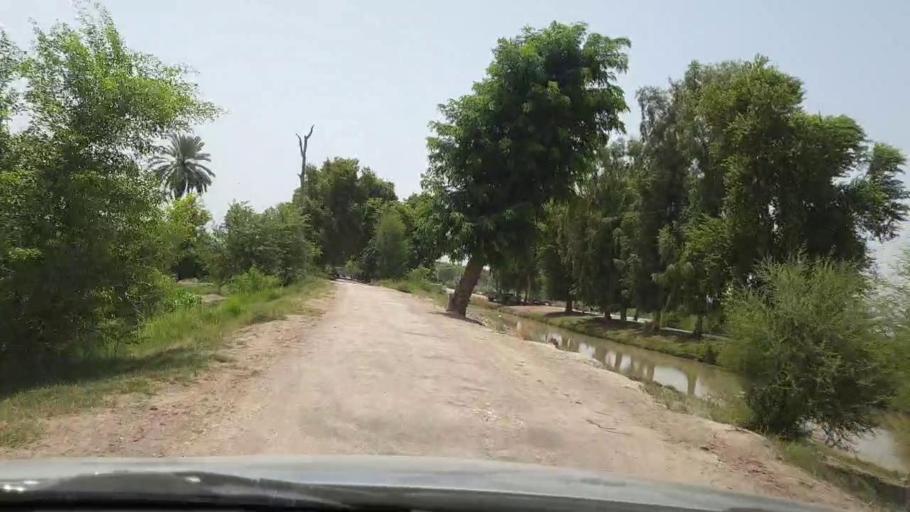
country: PK
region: Sindh
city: Pano Aqil
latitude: 27.8615
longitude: 69.0884
